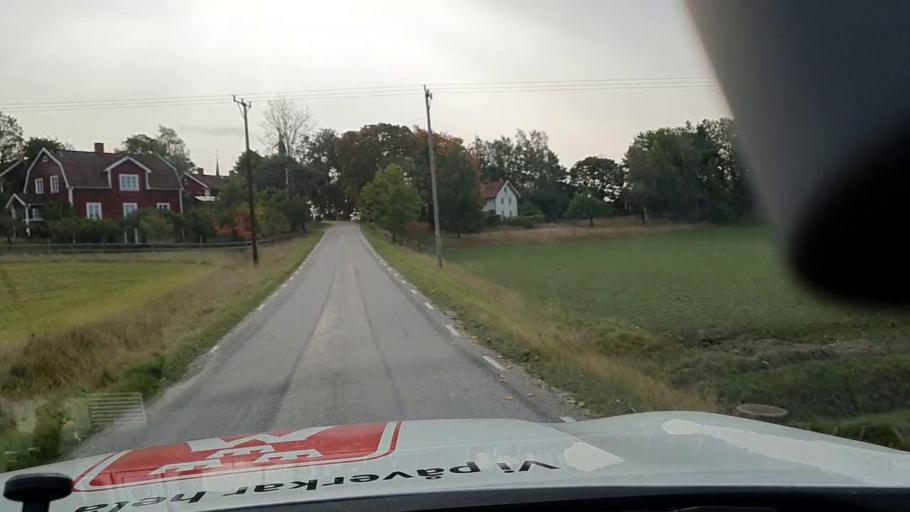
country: SE
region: Soedermanland
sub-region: Nykopings Kommun
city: Stigtomta
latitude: 58.9834
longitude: 16.9294
